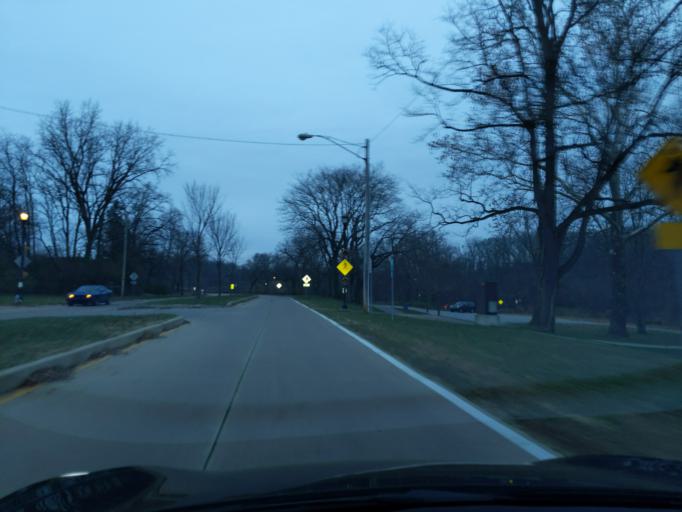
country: US
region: Indiana
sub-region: Saint Joseph County
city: Georgetown
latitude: 41.7276
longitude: -86.2693
